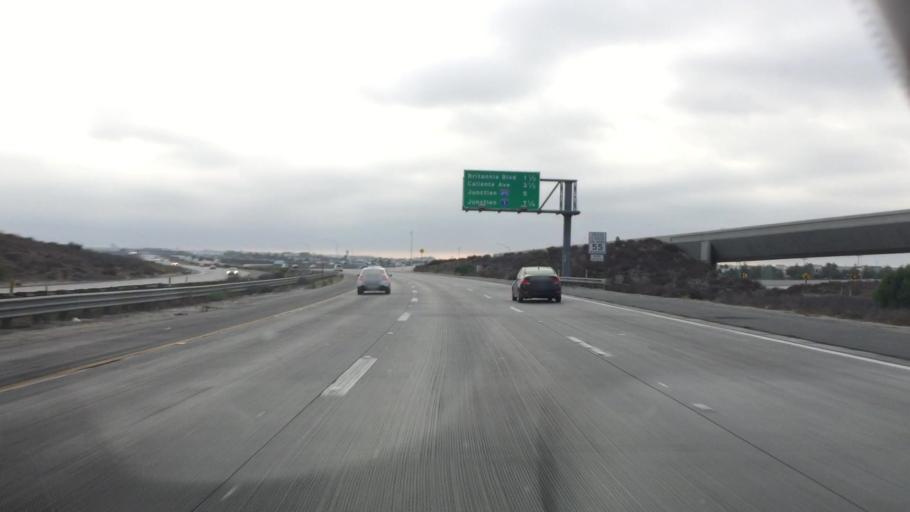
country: MX
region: Baja California
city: Tijuana
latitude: 32.5638
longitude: -116.9494
